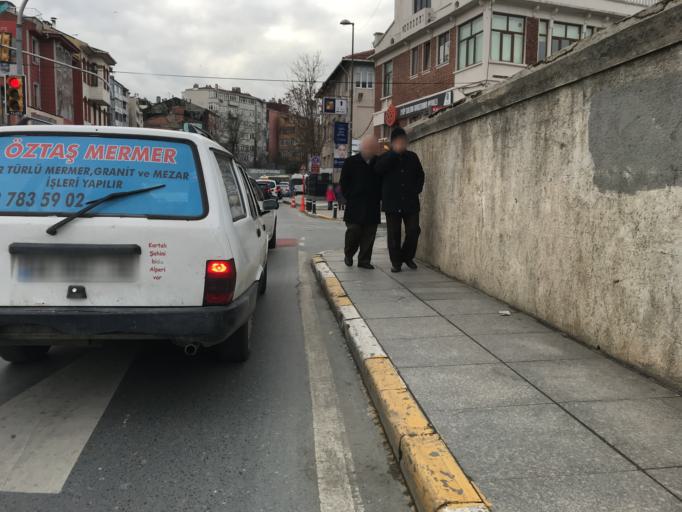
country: TR
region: Istanbul
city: Istanbul
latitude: 41.0462
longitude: 28.9347
